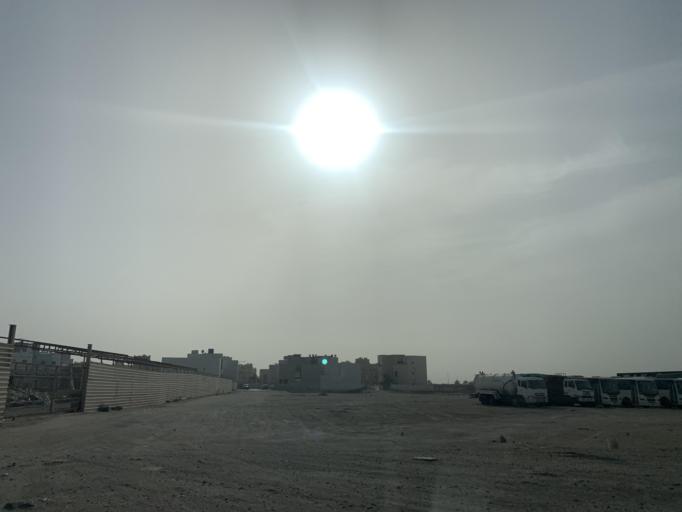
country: BH
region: Northern
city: Madinat `Isa
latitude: 26.1594
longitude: 50.5108
